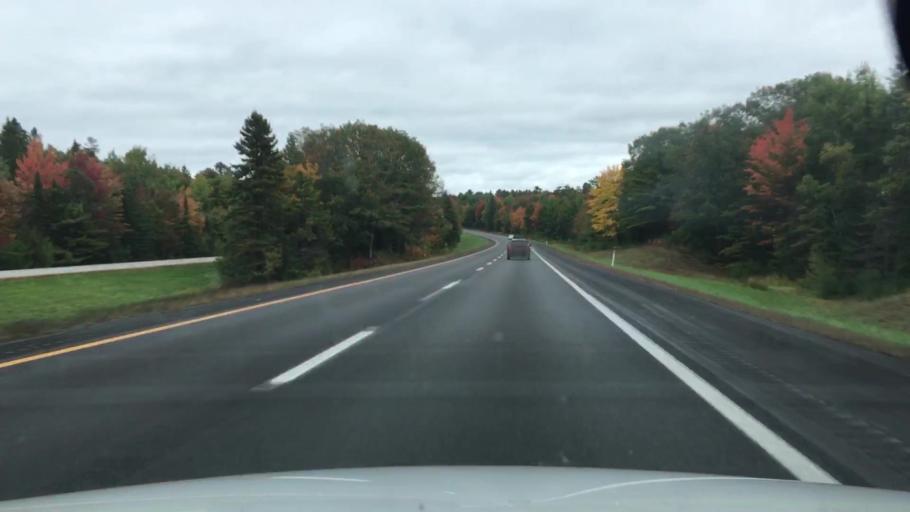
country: US
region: Maine
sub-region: Penobscot County
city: Veazie
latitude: 44.8617
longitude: -68.7144
